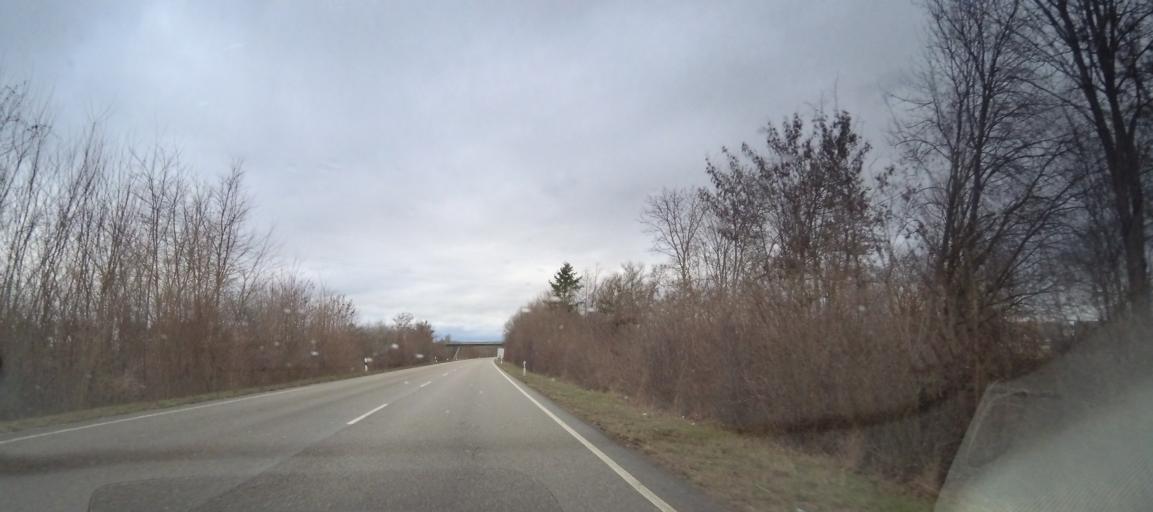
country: DE
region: Baden-Wuerttemberg
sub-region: Karlsruhe Region
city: Graben-Neudorf
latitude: 49.1931
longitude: 8.4640
